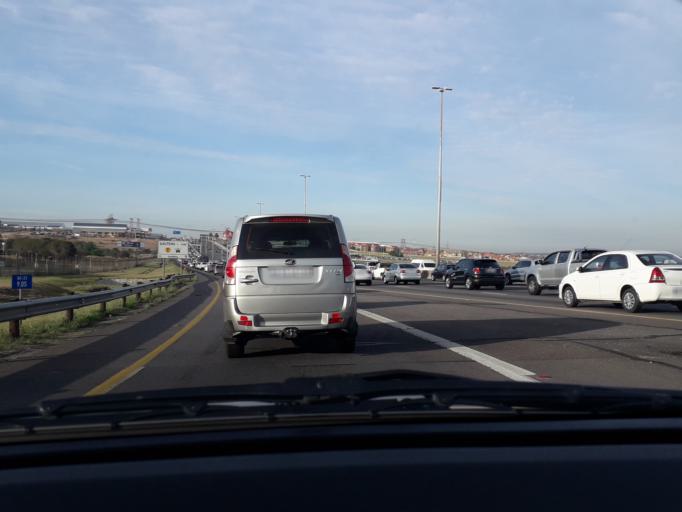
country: ZA
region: Gauteng
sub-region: City of Tshwane Metropolitan Municipality
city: Centurion
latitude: -25.9113
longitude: 28.1564
